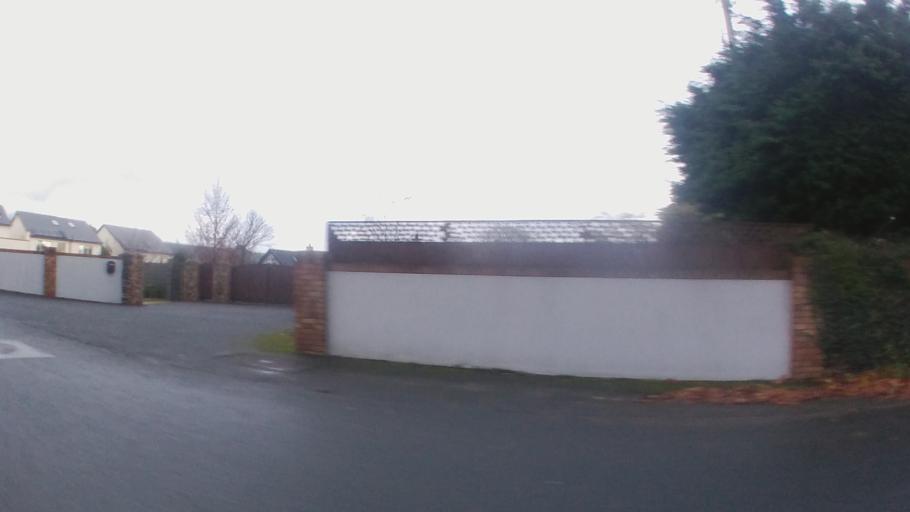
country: IE
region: Leinster
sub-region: Wicklow
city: Kilcoole
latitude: 53.1103
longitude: -6.0612
